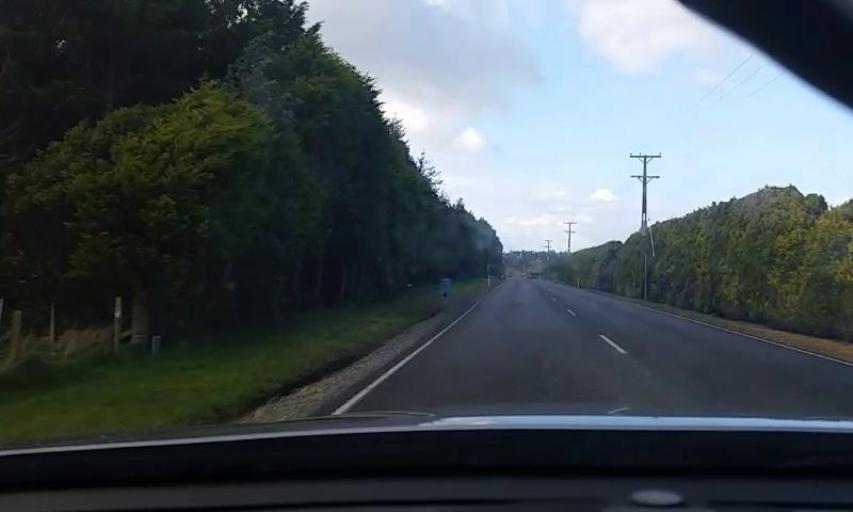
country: NZ
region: Southland
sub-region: Invercargill City
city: Invercargill
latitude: -46.3806
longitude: 168.4298
